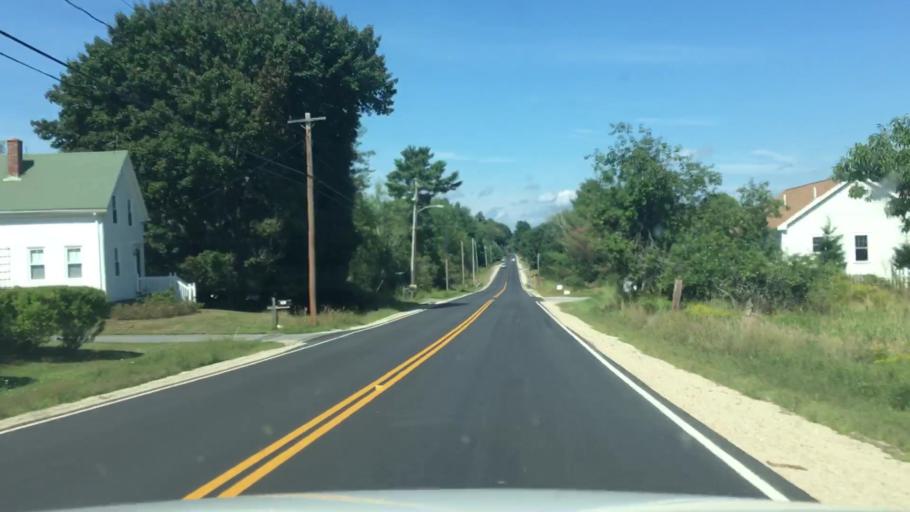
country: US
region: Maine
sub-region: Cumberland County
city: Cumberland Center
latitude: 43.7878
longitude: -70.3048
